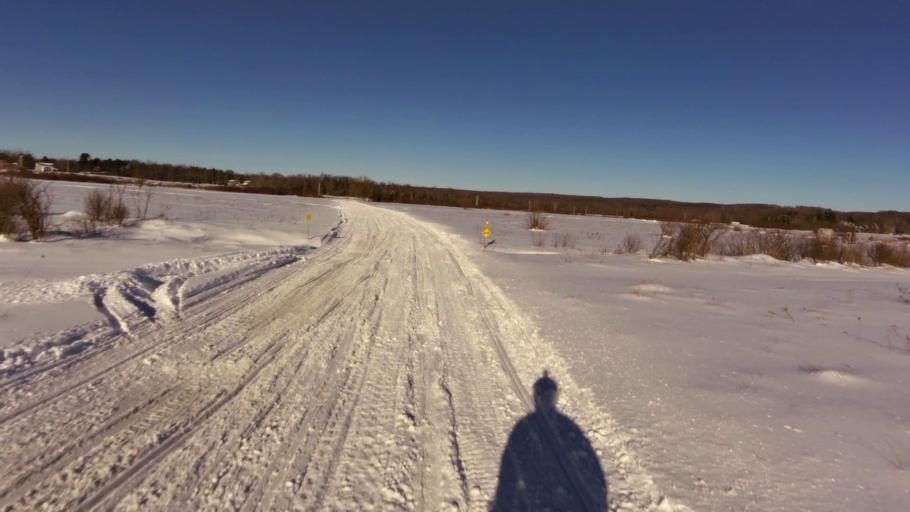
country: US
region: New York
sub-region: Chautauqua County
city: Mayville
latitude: 42.2699
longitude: -79.4889
